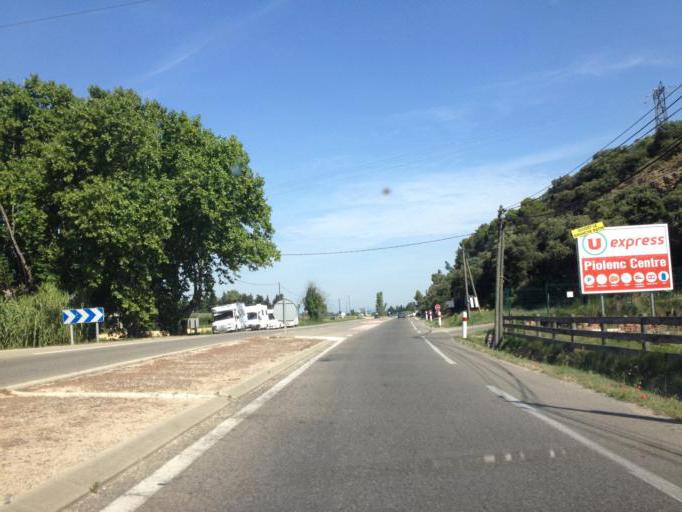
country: FR
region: Provence-Alpes-Cote d'Azur
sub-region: Departement du Vaucluse
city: Piolenc
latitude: 44.1653
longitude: 4.7674
